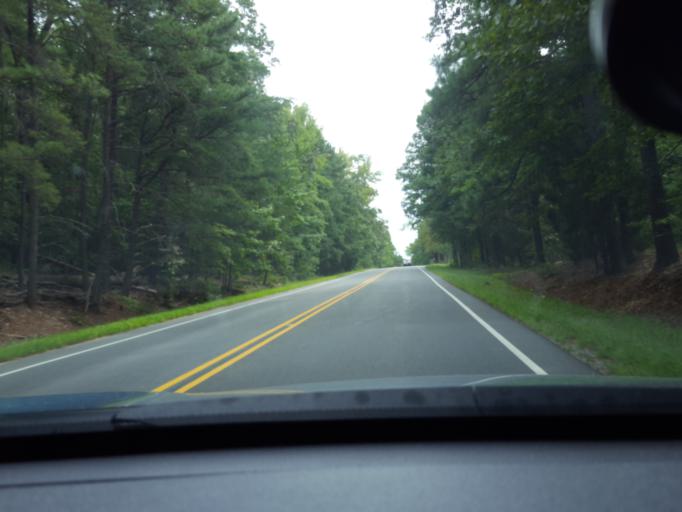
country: US
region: Virginia
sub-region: Caroline County
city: Bowling Green
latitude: 37.9958
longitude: -77.3362
